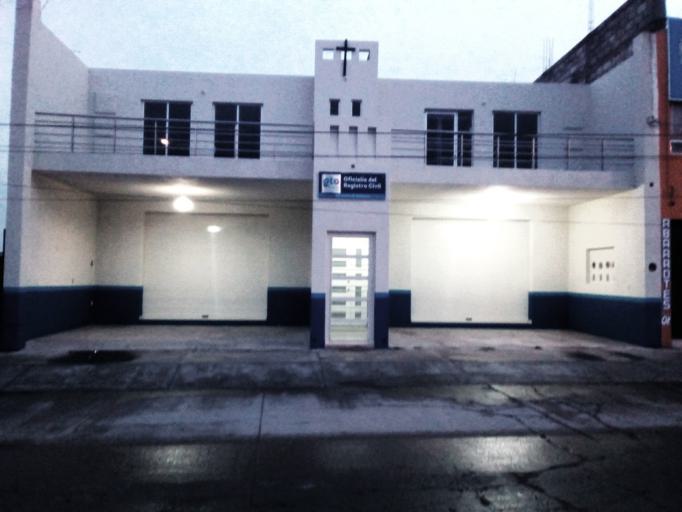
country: MX
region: Guerrero
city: San Luis de la Paz
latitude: 21.2895
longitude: -100.5197
